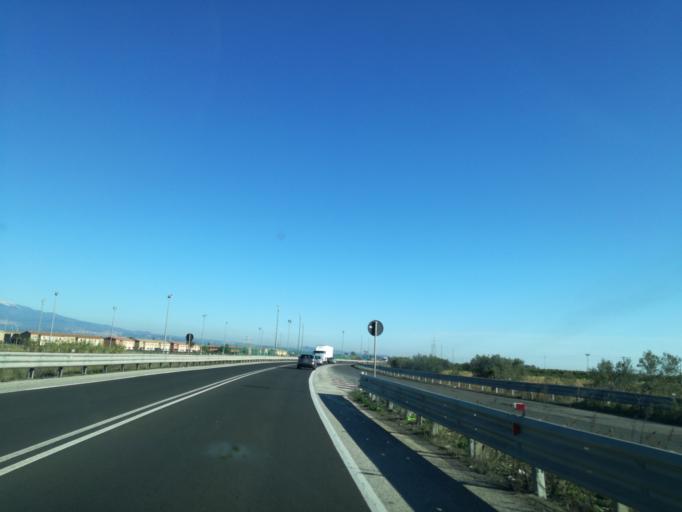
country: IT
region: Sicily
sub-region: Catania
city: Motta Sant'Anastasia
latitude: 37.4169
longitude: 14.9095
